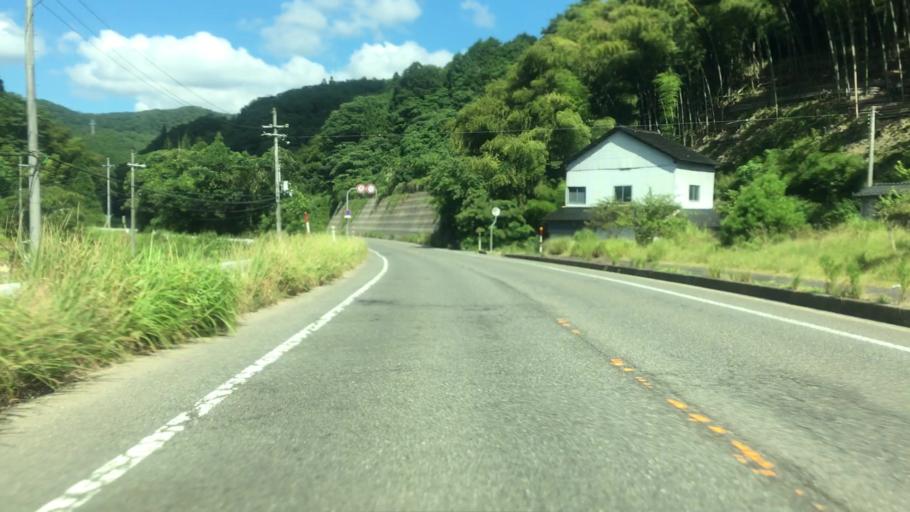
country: JP
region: Hyogo
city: Toyooka
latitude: 35.5755
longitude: 134.7635
